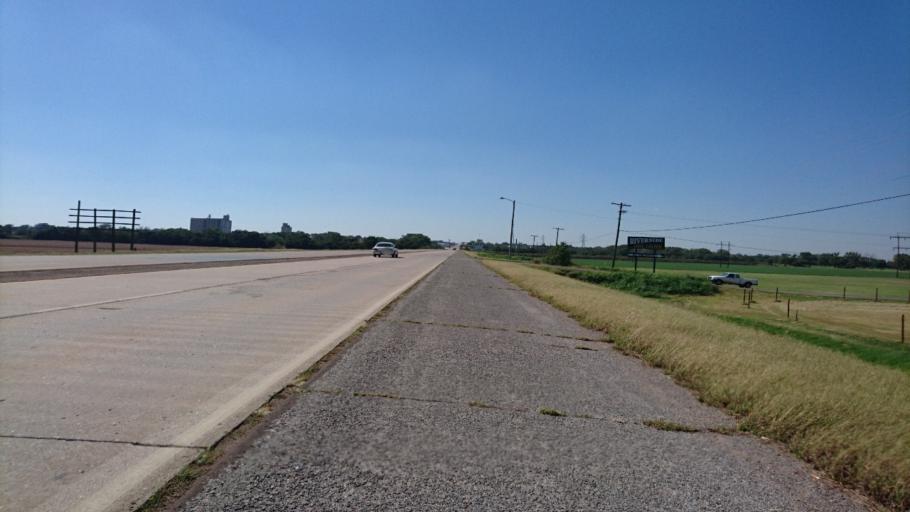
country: US
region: Oklahoma
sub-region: Custer County
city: Clinton
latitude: 35.5158
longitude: -98.9485
